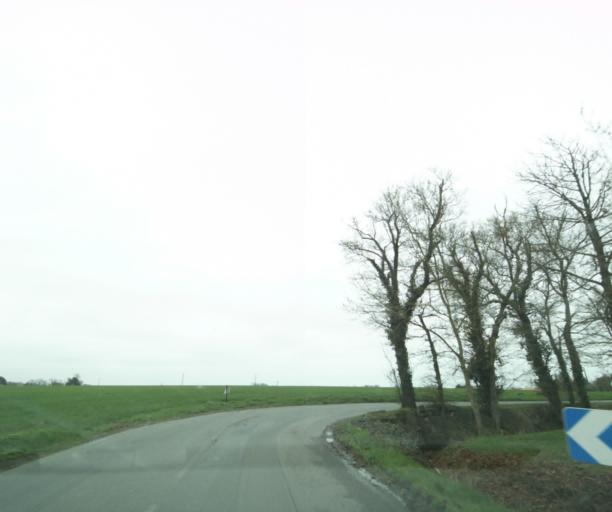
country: FR
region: Poitou-Charentes
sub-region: Departement de la Charente-Maritime
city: Lagord
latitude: 46.1897
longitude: -1.1377
